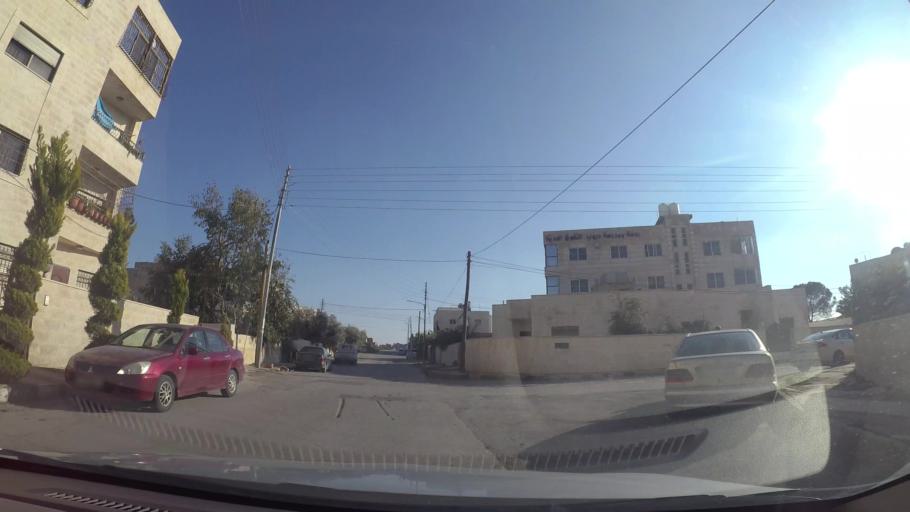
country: JO
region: Amman
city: Al Bunayyat ash Shamaliyah
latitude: 31.8994
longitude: 35.9204
